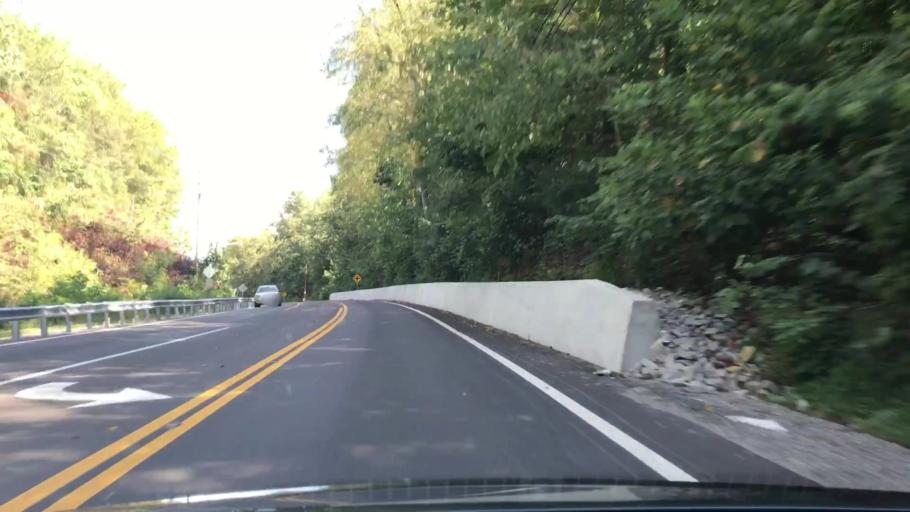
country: US
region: Alabama
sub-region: Limestone County
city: Ardmore
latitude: 35.0026
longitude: -86.8685
